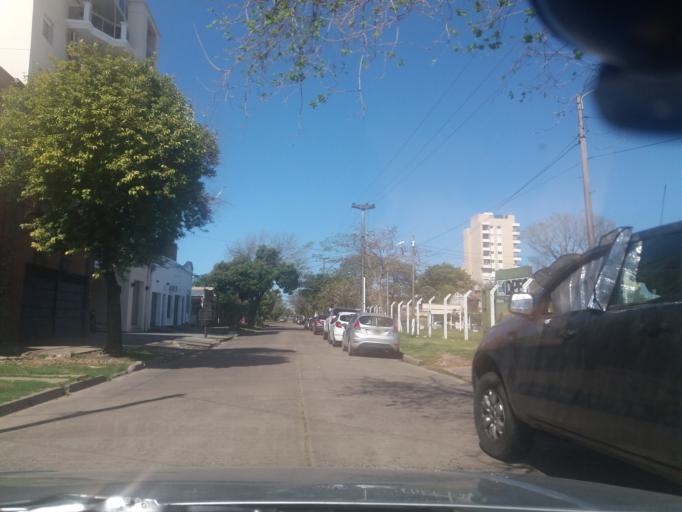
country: AR
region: Corrientes
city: Corrientes
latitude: -27.4701
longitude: -58.8496
